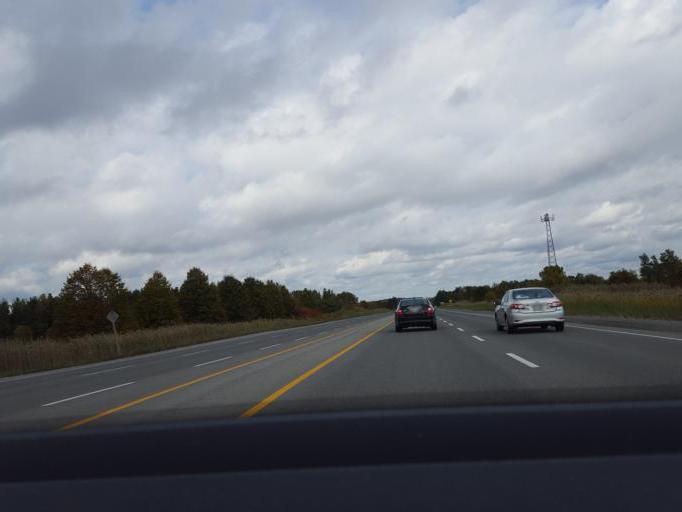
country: CA
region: Ontario
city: Pickering
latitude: 43.8652
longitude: -79.1447
